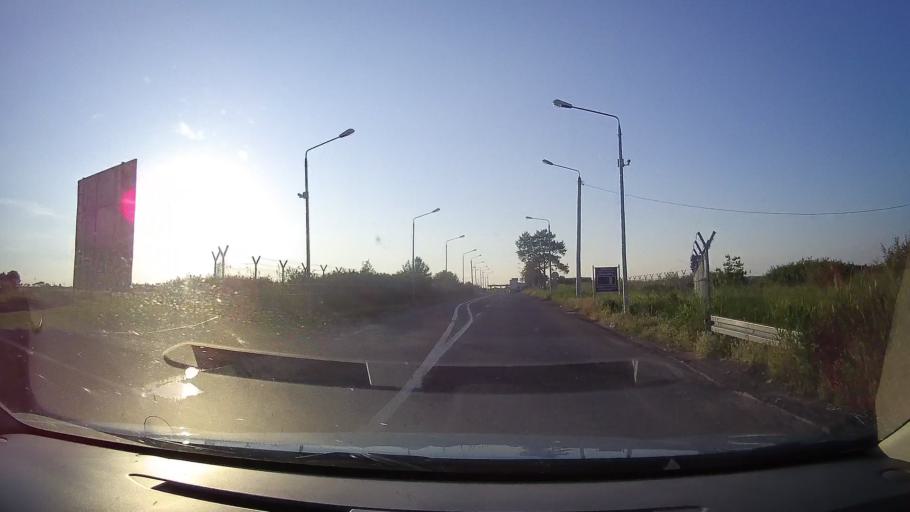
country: RO
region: Timis
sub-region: Comuna Moravita
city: Moravita
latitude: 45.2295
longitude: 21.2752
